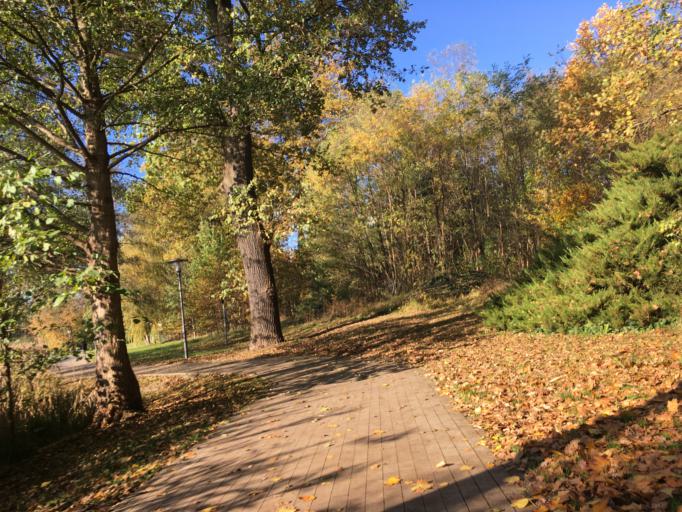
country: DE
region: Brandenburg
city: Bad Saarow
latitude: 52.2909
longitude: 14.0535
